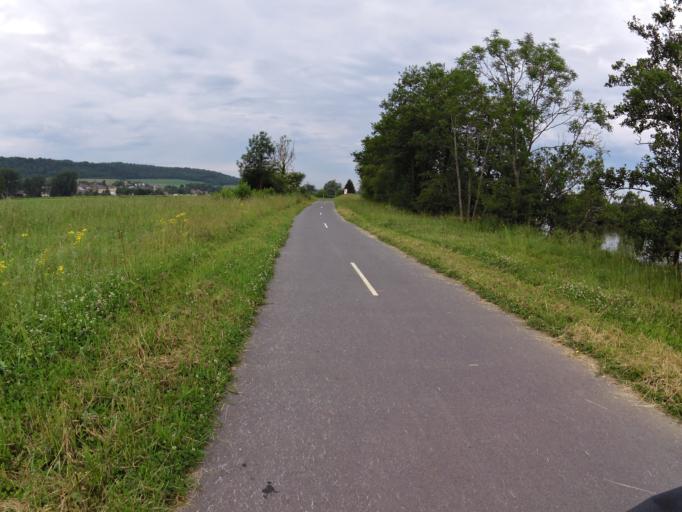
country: FR
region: Champagne-Ardenne
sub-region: Departement des Ardennes
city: Dom-le-Mesnil
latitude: 49.6932
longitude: 4.8206
